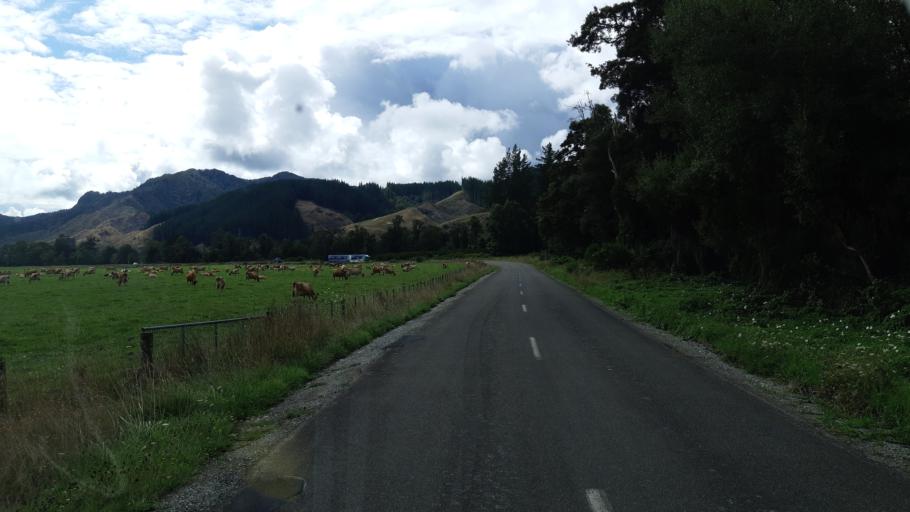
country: NZ
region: West Coast
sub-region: Buller District
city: Westport
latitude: -41.7736
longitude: 172.3747
